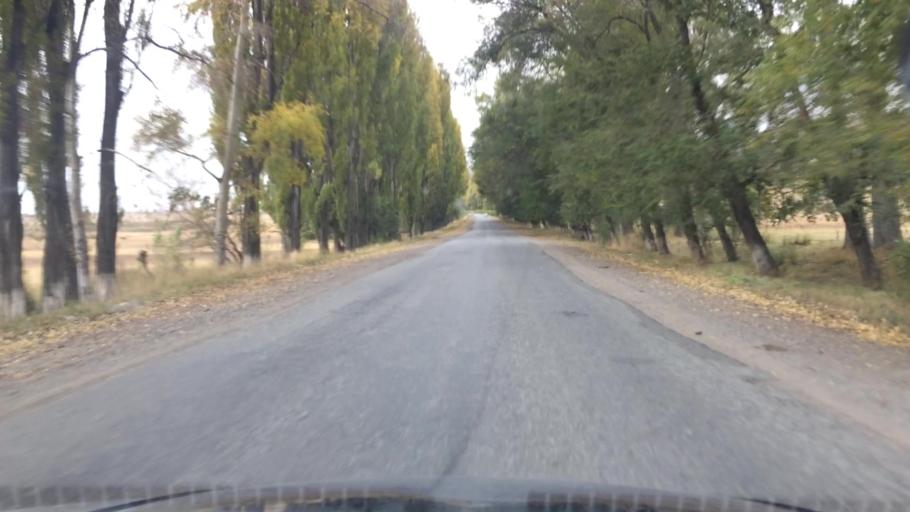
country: KG
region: Ysyk-Koel
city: Pokrovka
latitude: 42.7391
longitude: 77.9115
